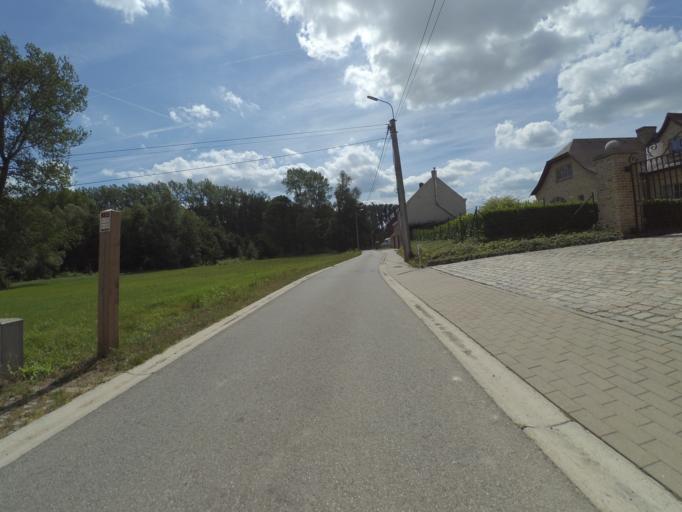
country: BE
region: Flanders
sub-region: Provincie Oost-Vlaanderen
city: Zottegem
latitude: 50.8520
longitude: 3.7627
